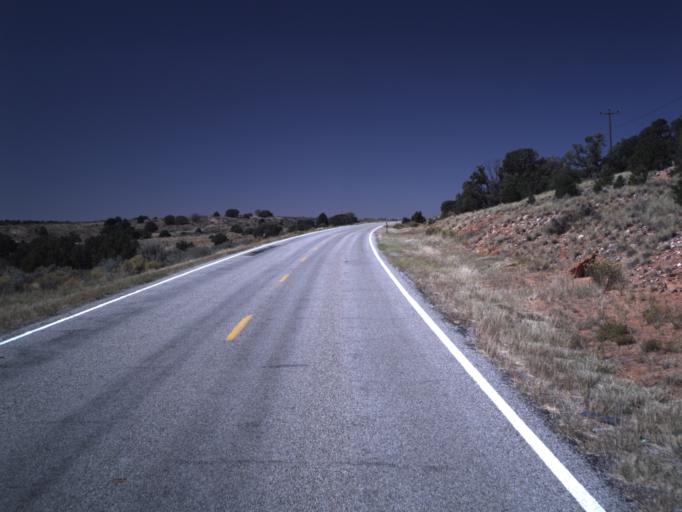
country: US
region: Utah
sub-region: Grand County
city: Moab
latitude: 38.3056
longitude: -109.3925
